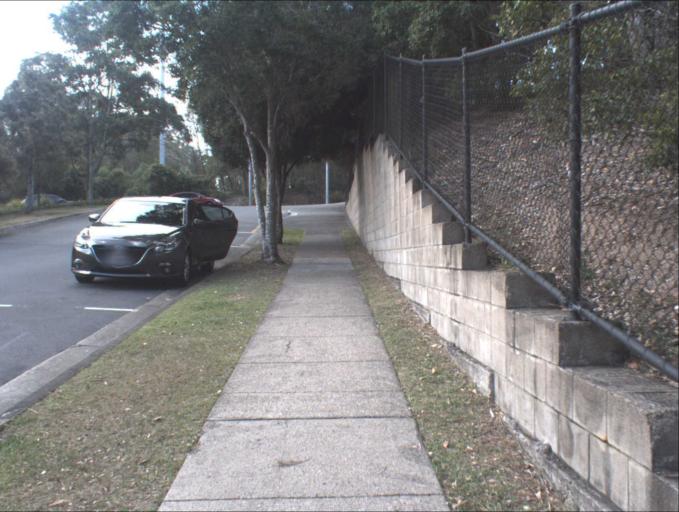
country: AU
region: Queensland
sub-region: Logan
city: Slacks Creek
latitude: -27.6328
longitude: 153.1482
